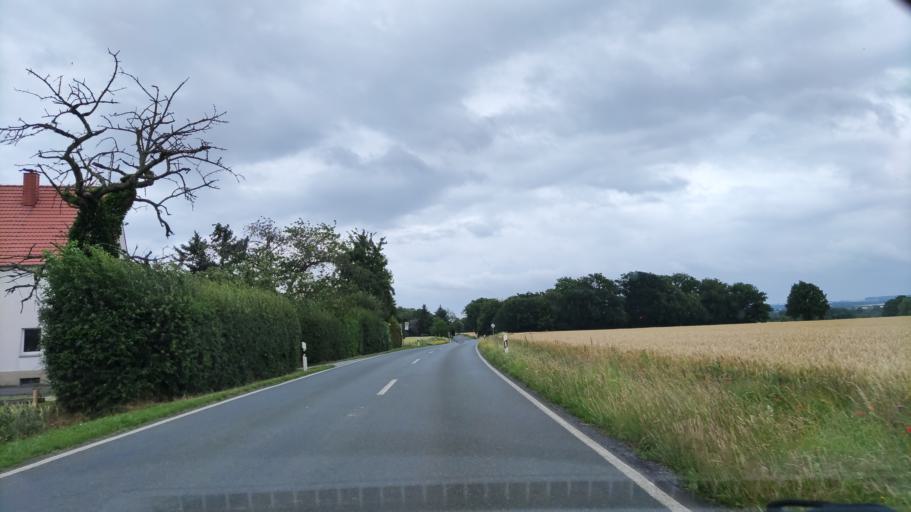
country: DE
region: North Rhine-Westphalia
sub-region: Regierungsbezirk Arnsberg
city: Soest
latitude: 51.5928
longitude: 8.0750
